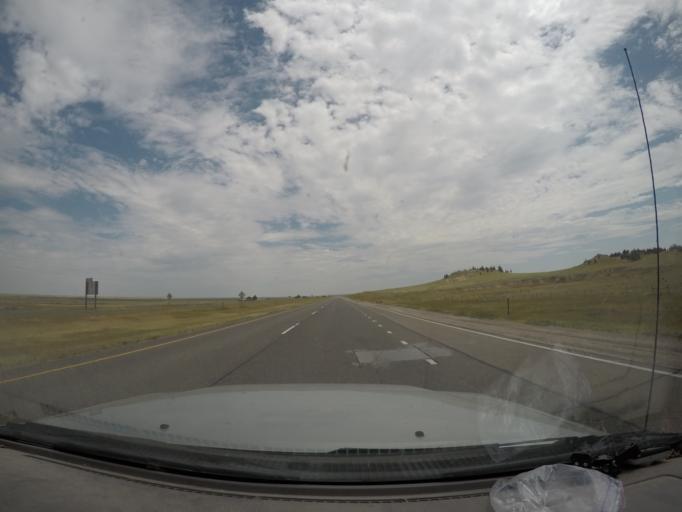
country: US
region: Wyoming
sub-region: Laramie County
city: Pine Bluffs
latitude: 41.1840
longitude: -104.0384
